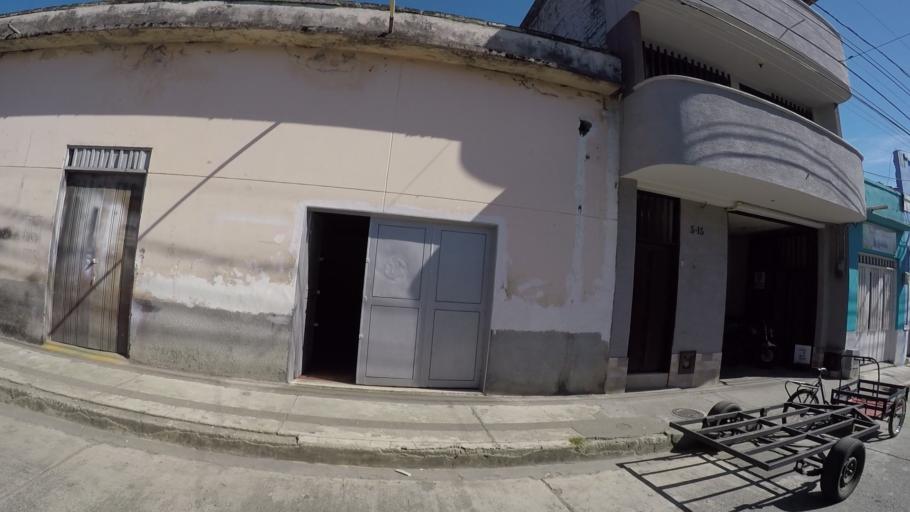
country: CO
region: Valle del Cauca
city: Cartago
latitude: 4.7486
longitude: -75.9065
